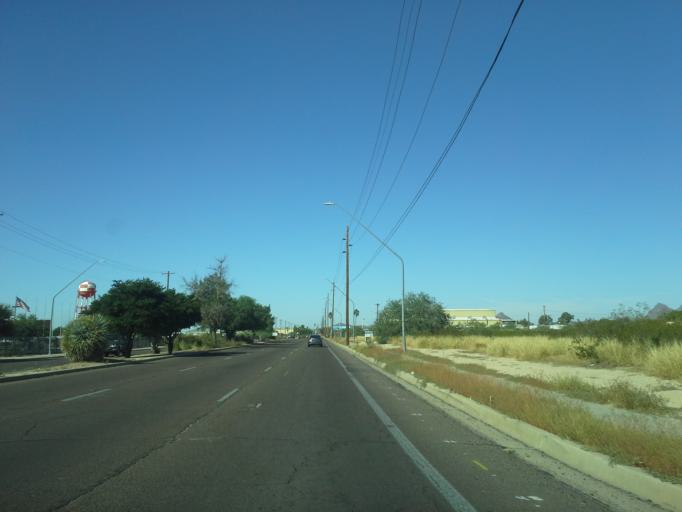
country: US
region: Arizona
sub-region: Pima County
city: Summit
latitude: 32.1342
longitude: -110.9458
